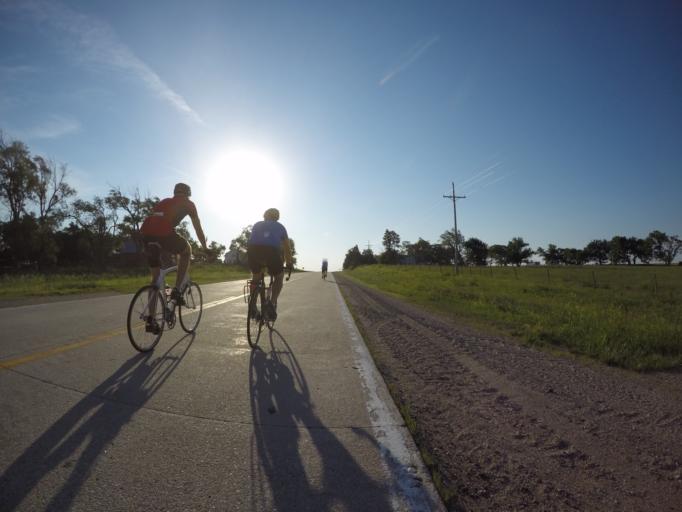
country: US
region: Nebraska
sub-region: Gage County
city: Wymore
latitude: 40.0448
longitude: -96.6190
